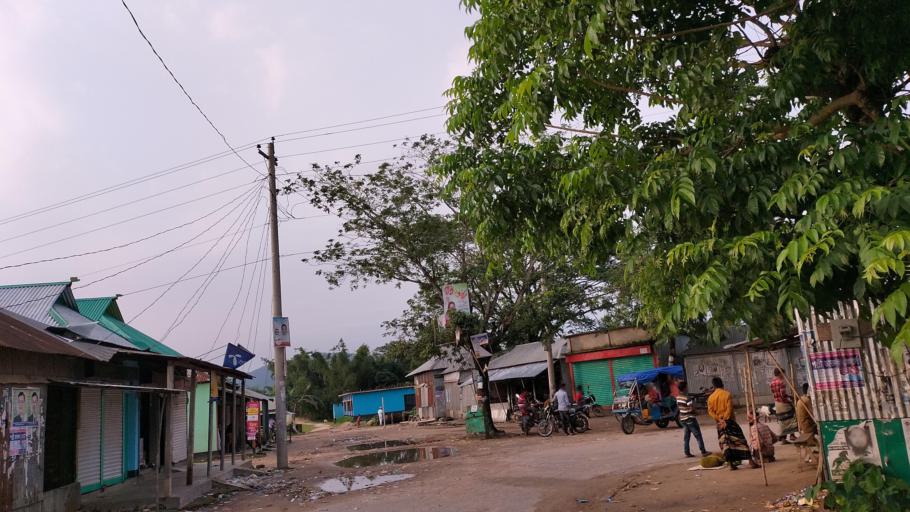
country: BD
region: Dhaka
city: Netrakona
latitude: 25.1344
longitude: 90.9137
